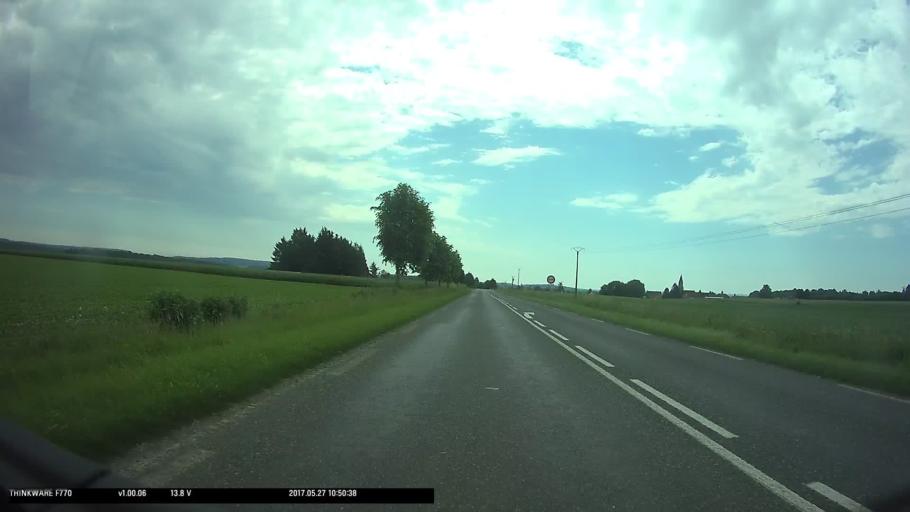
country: FR
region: Ile-de-France
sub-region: Departement du Val-d'Oise
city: Chars
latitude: 49.1812
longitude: 1.8995
